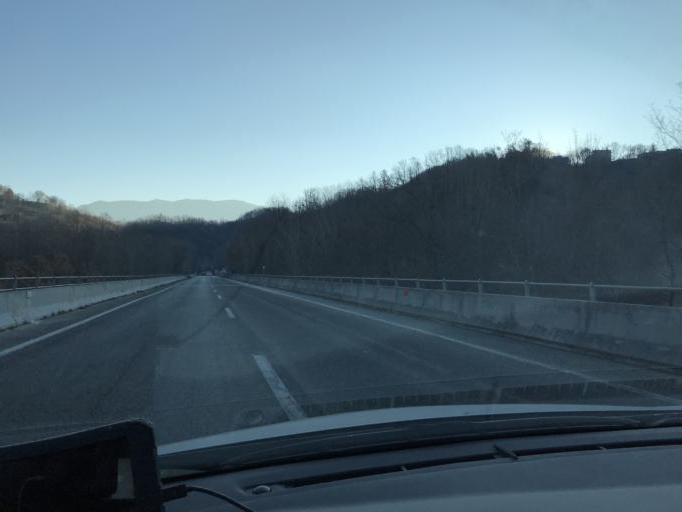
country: IT
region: Latium
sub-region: Provincia di Rieti
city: Fiamignano
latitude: 42.2545
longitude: 13.1432
